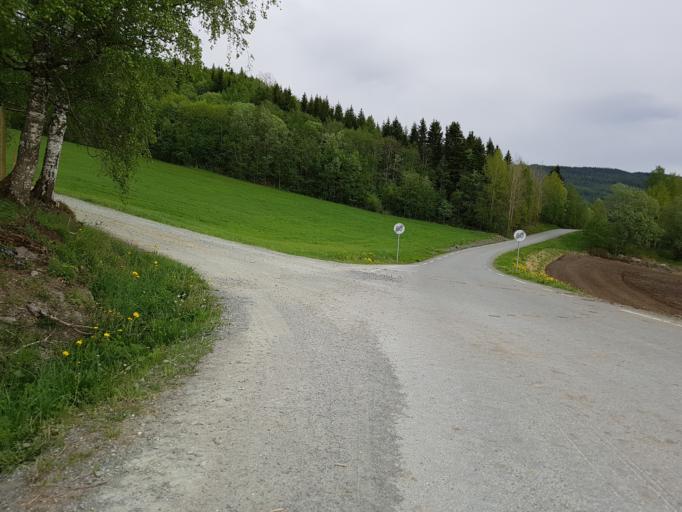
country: NO
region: Nord-Trondelag
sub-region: Levanger
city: Skogn
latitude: 63.6236
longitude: 11.2775
